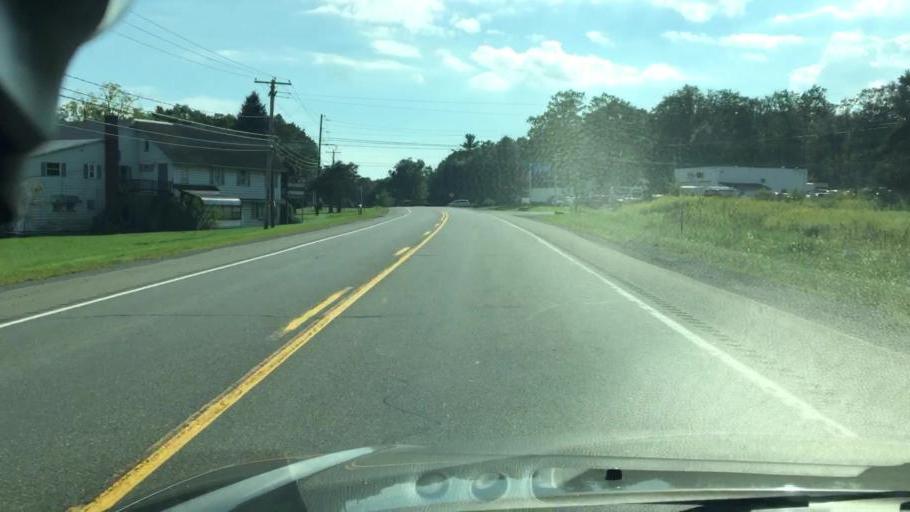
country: US
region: Pennsylvania
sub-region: Carbon County
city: Towamensing Trails
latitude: 40.9710
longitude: -75.6426
